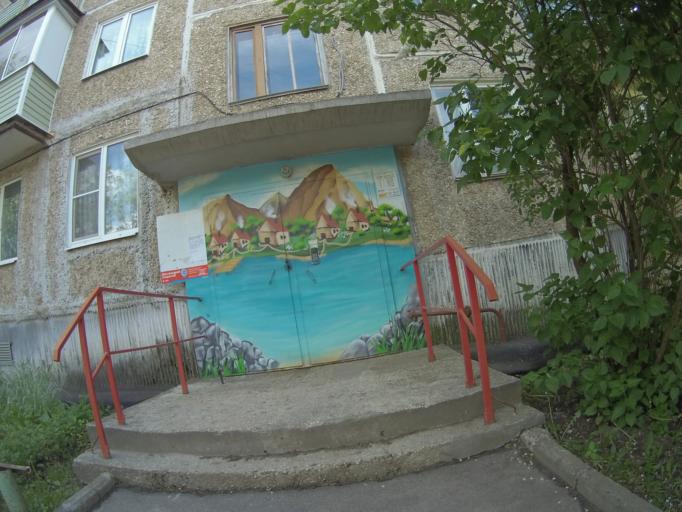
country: RU
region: Vladimir
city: Vladimir
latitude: 56.1252
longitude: 40.3477
